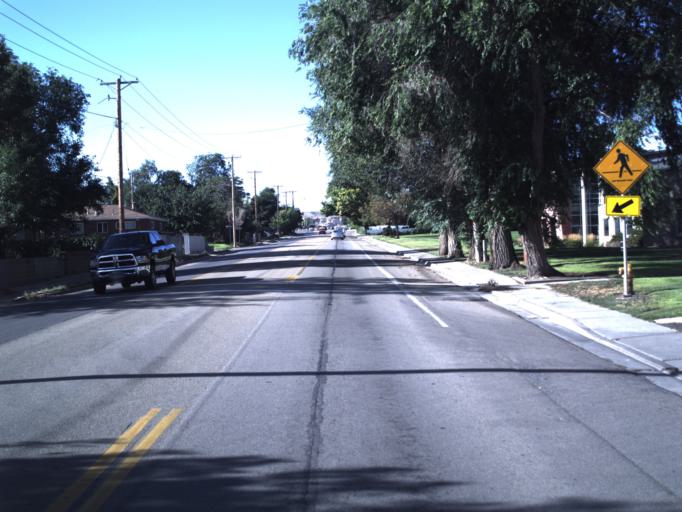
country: US
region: Utah
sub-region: Salt Lake County
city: Magna
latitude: 40.7007
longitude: -112.0919
